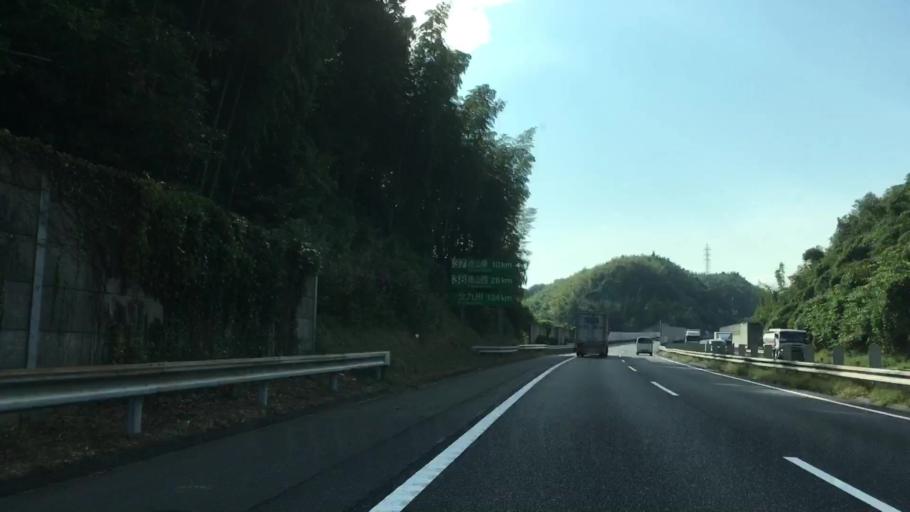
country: JP
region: Yamaguchi
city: Hikari
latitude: 34.0271
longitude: 131.9565
